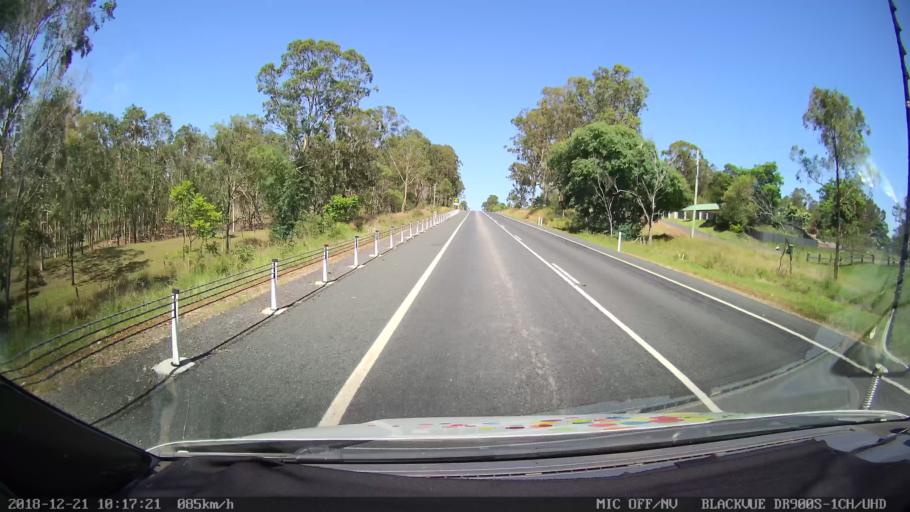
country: AU
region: New South Wales
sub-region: Clarence Valley
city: South Grafton
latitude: -29.6838
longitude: 152.8718
